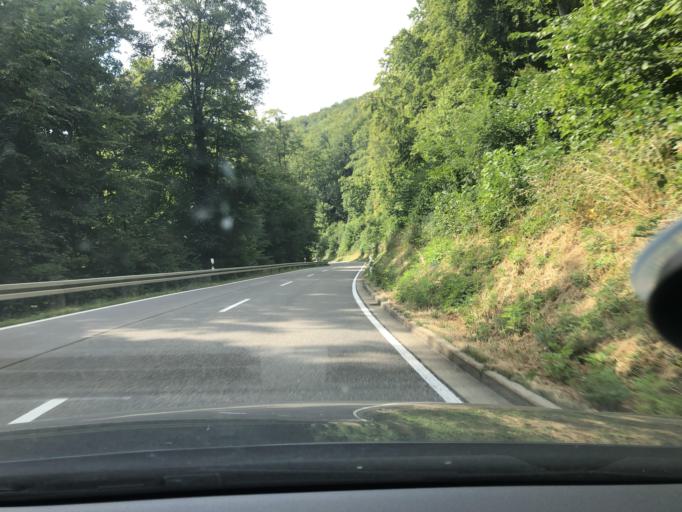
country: DE
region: Baden-Wuerttemberg
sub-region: Tuebingen Region
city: Pfullingen
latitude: 48.4327
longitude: 9.2036
